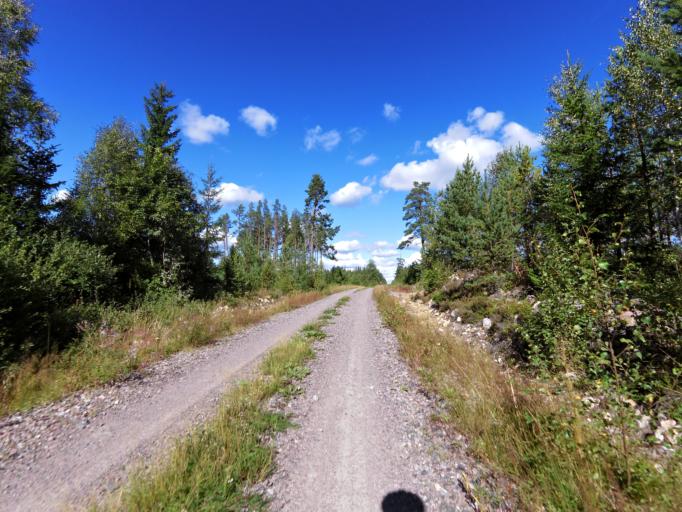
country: SE
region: Gaevleborg
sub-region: Gavle Kommun
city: Valbo
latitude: 60.7411
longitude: 16.9837
